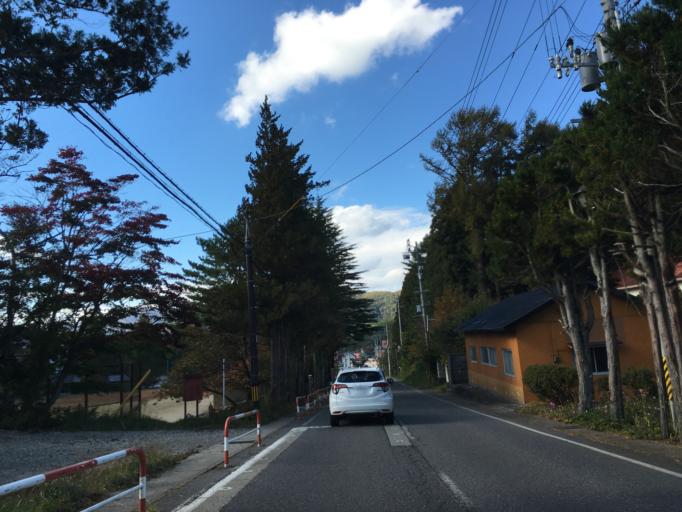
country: JP
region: Fukushima
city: Inawashiro
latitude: 37.6154
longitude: 140.2065
